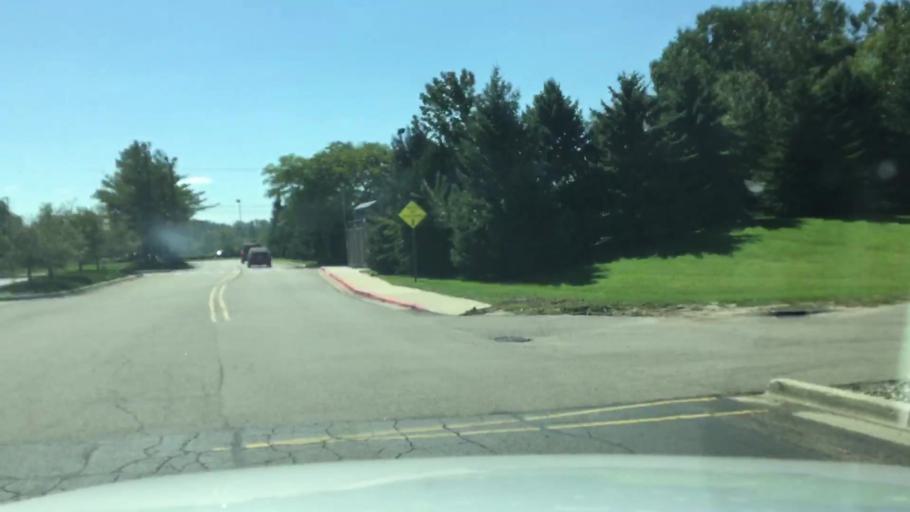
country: US
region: Michigan
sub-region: Kalamazoo County
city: Portage
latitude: 42.2168
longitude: -85.5912
